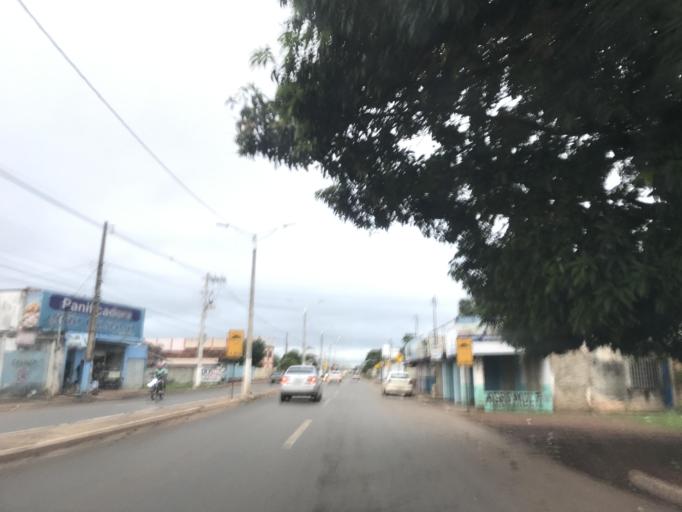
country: BR
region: Goias
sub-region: Luziania
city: Luziania
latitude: -16.2083
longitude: -47.9268
